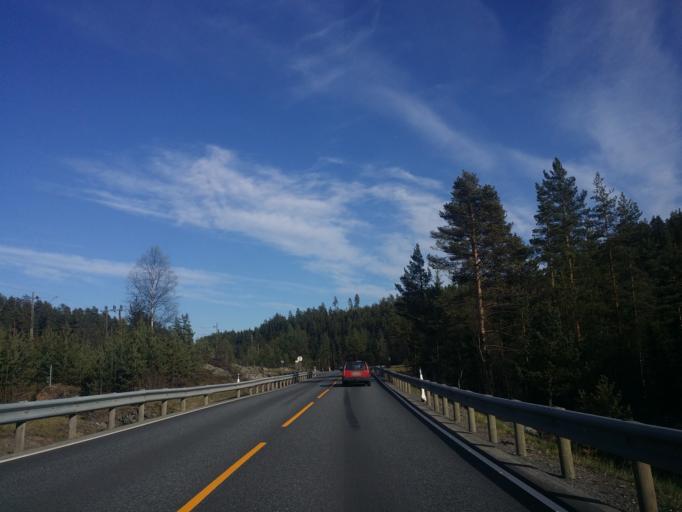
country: NO
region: Buskerud
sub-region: Kongsberg
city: Kongsberg
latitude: 59.6300
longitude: 9.5415
